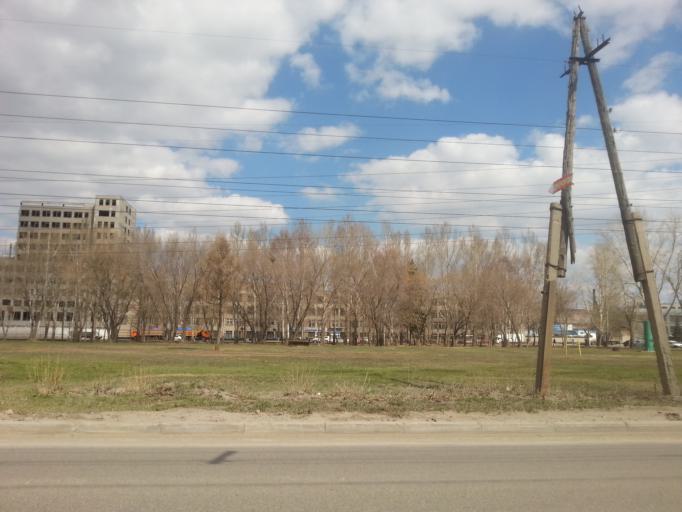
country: RU
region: Altai Krai
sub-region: Gorod Barnaulskiy
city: Barnaul
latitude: 53.3861
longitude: 83.7202
